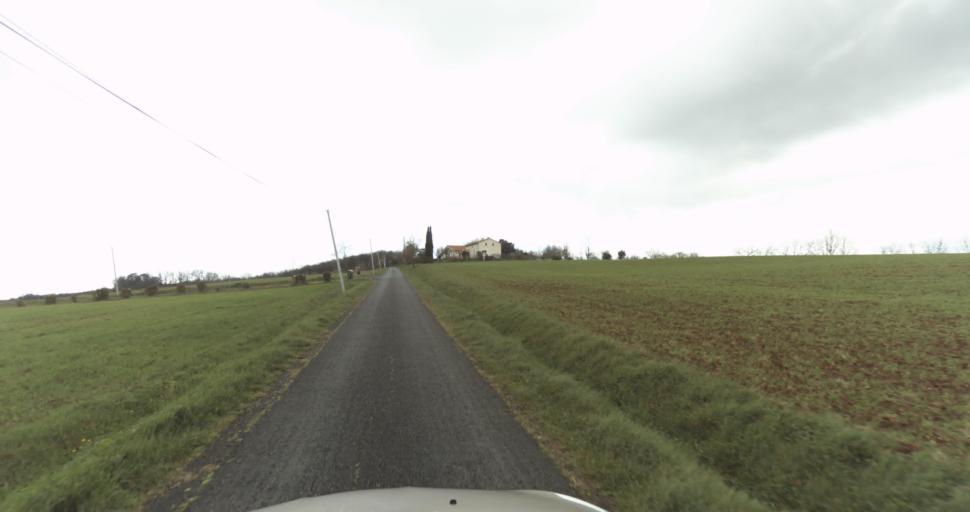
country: FR
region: Midi-Pyrenees
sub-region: Departement du Tarn
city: Frejairolles
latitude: 43.8609
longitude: 2.2080
